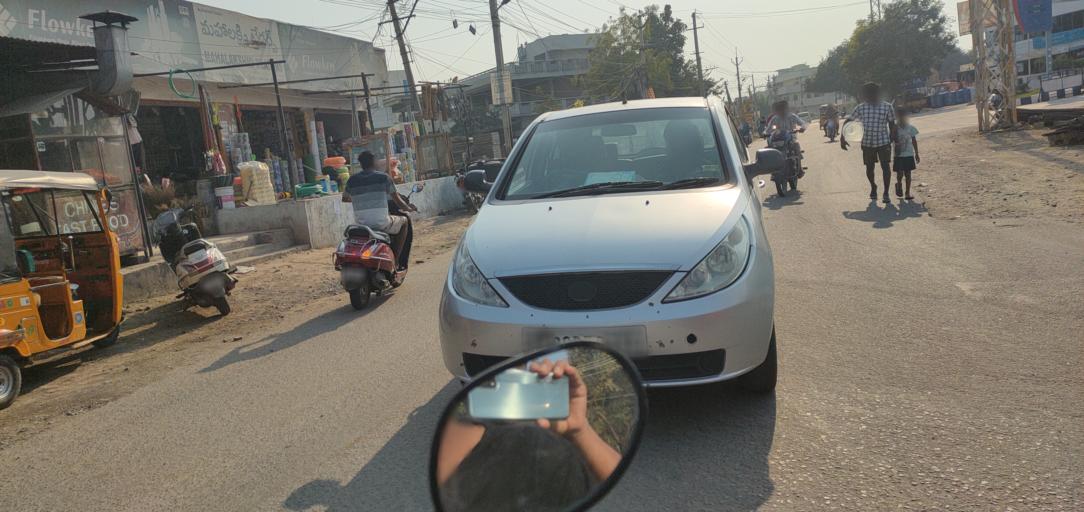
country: IN
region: Telangana
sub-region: Rangareddi
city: Lal Bahadur Nagar
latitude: 17.3395
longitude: 78.6245
